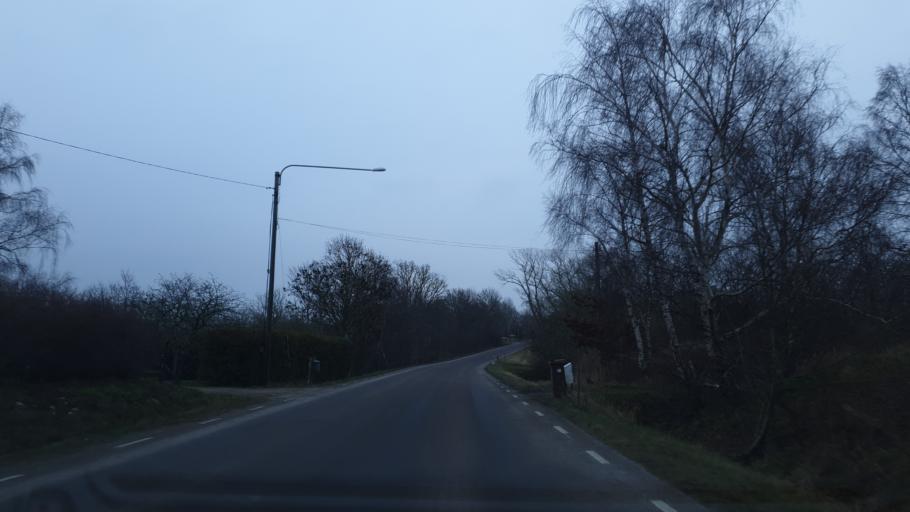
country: SE
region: Blekinge
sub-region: Karlskrona Kommun
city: Sturko
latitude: 56.1130
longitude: 15.6975
